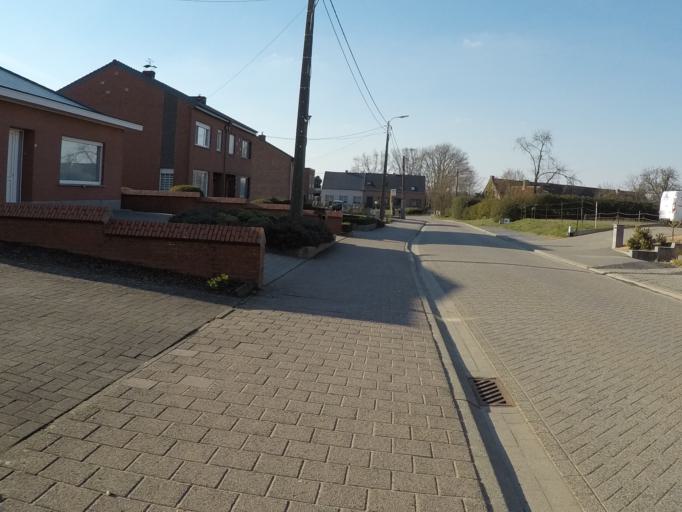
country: BE
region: Flanders
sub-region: Provincie Antwerpen
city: Heist-op-den-Berg
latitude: 51.0796
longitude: 4.7062
